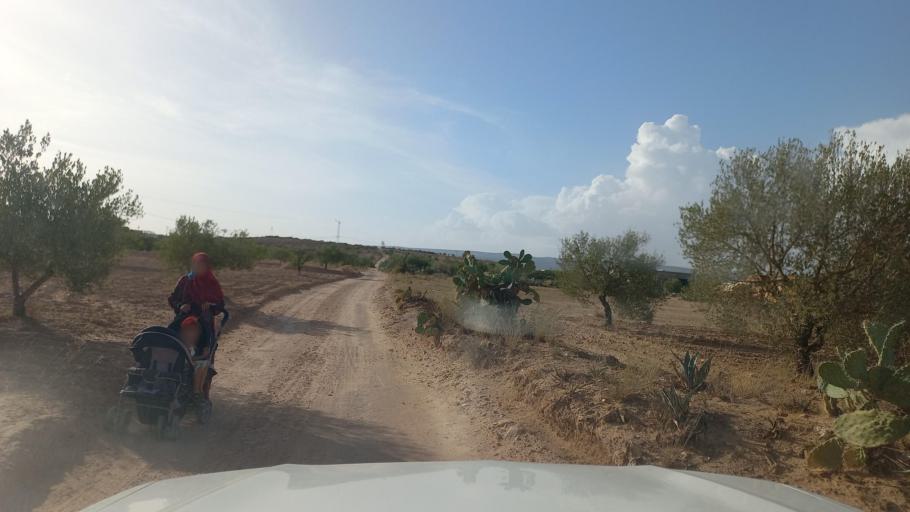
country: TN
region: Al Qasrayn
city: Kasserine
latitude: 35.2323
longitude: 8.9221
